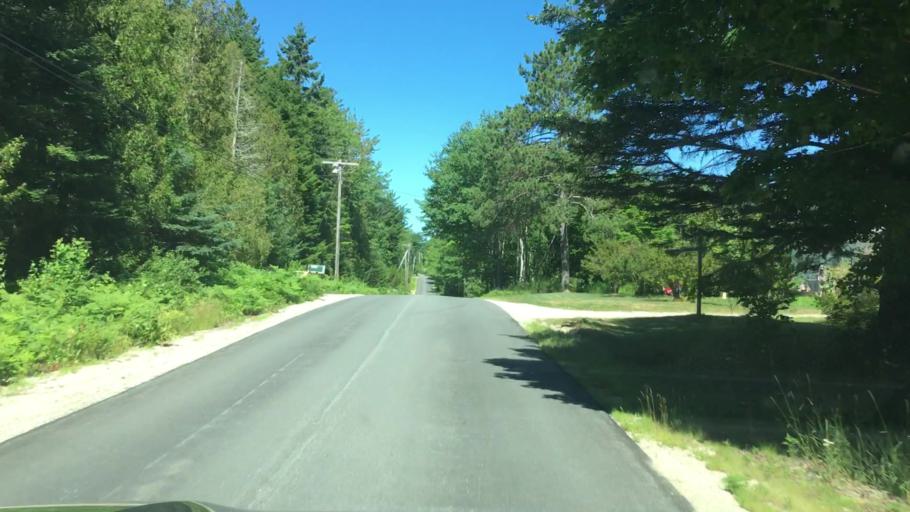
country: US
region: Maine
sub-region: Hancock County
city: Sedgwick
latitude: 44.3188
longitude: -68.6260
